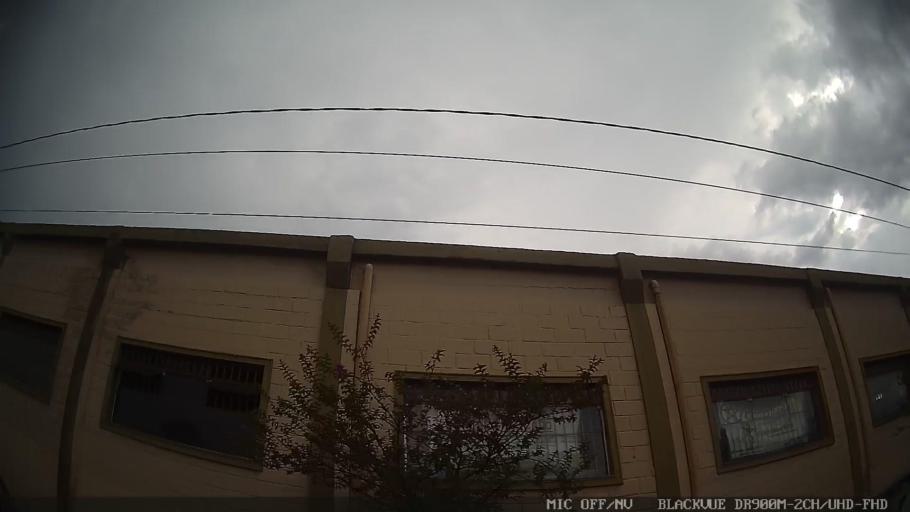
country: BR
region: Sao Paulo
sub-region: Itatiba
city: Itatiba
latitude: -23.0080
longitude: -46.8430
